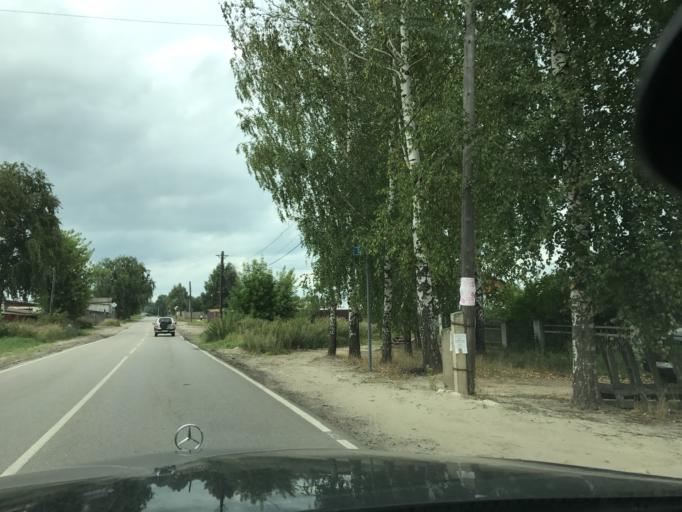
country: RU
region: Nizjnij Novgorod
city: Taremskoye
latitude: 55.9962
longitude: 43.0105
